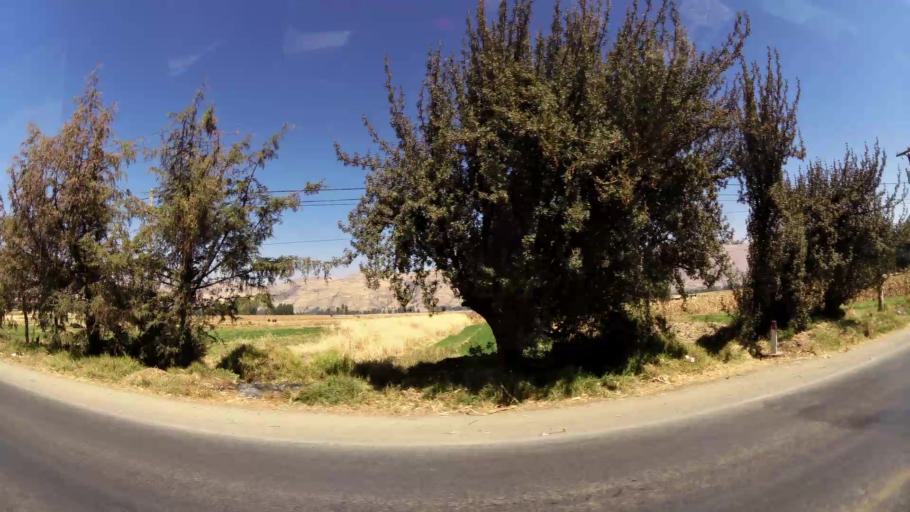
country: PE
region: Junin
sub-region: Provincia de Jauja
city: San Lorenzo
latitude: -11.8524
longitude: -75.3814
